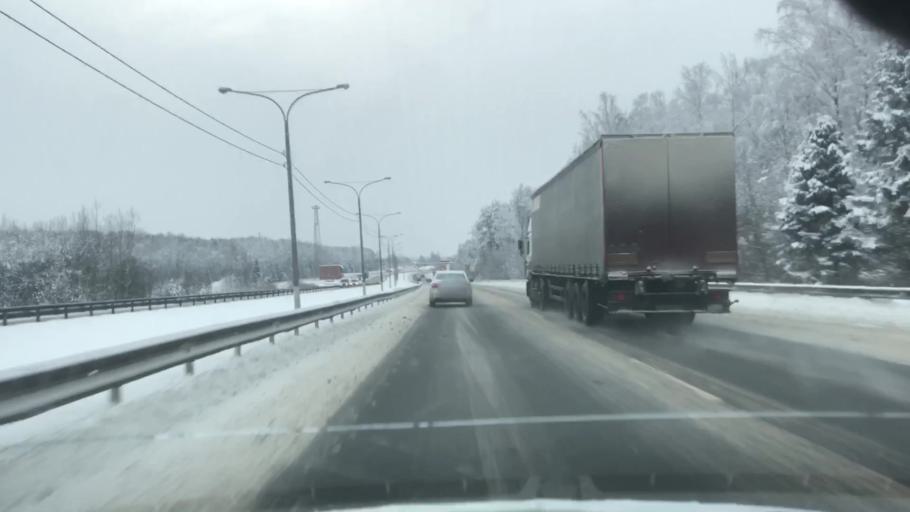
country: RU
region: Moskovskaya
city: Mikhnevo
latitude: 55.1380
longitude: 37.9324
